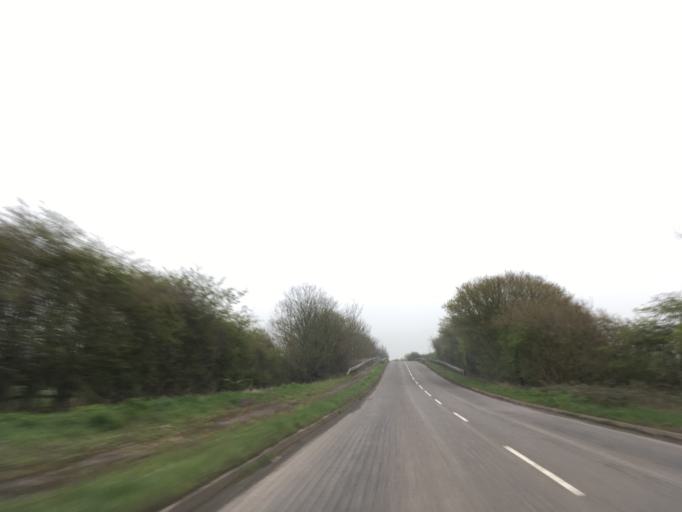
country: GB
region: England
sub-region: South Gloucestershire
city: Almondsbury
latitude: 51.5569
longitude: -2.5415
